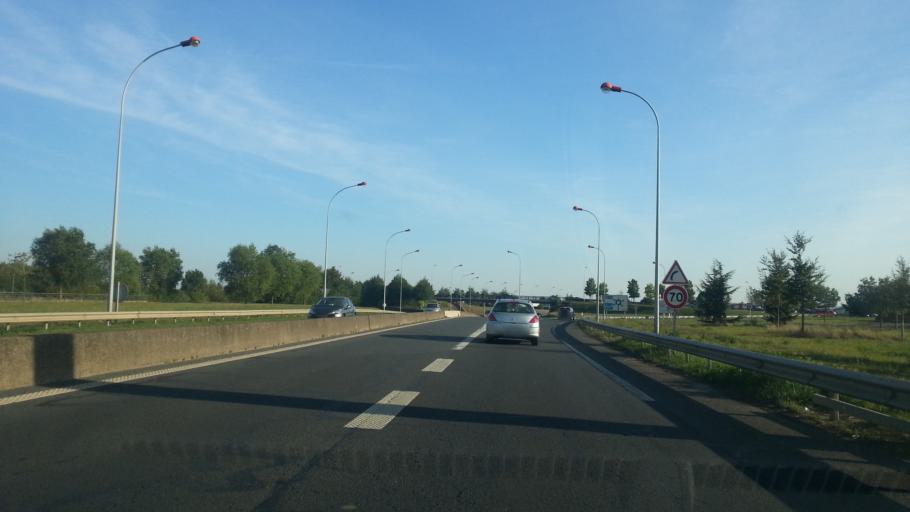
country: FR
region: Picardie
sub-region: Departement de l'Oise
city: Allonne
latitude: 49.4345
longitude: 2.1167
